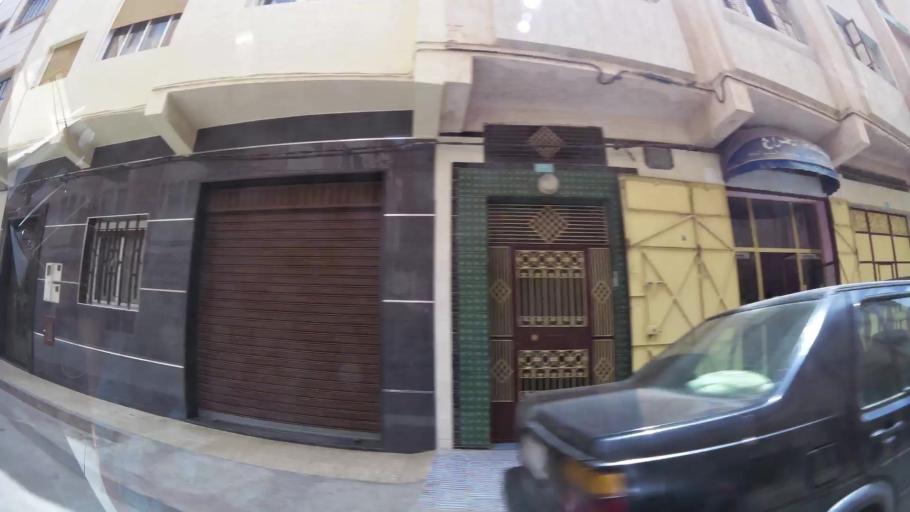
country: MA
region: Oriental
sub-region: Nador
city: Nador
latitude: 35.1684
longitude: -2.9220
